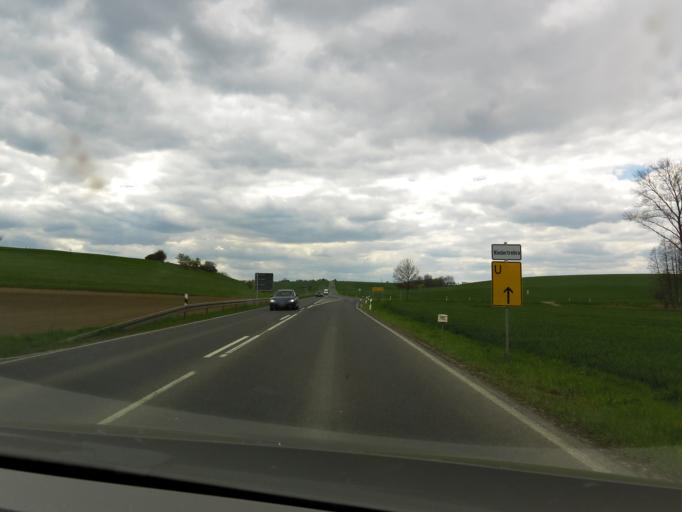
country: DE
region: Thuringia
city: Rannstedt
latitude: 51.0996
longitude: 11.5467
